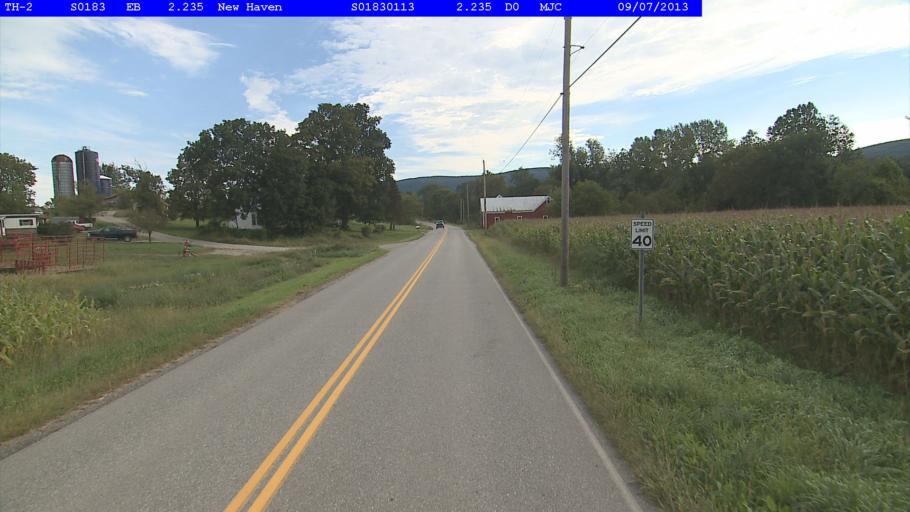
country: US
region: Vermont
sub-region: Addison County
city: Middlebury (village)
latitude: 44.0728
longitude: -73.1333
